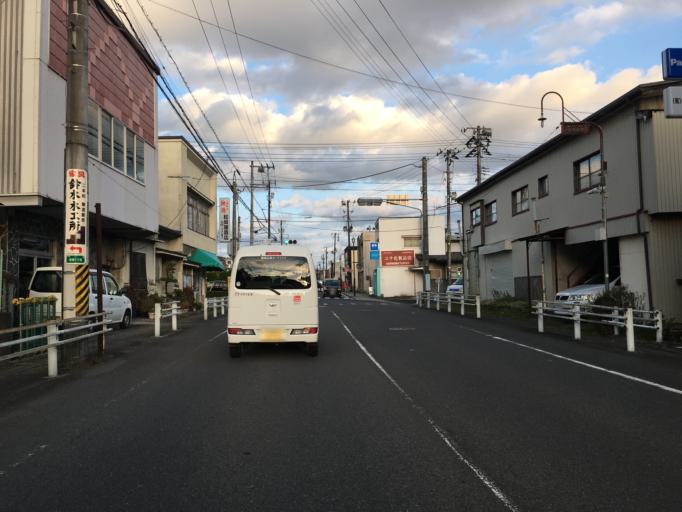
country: JP
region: Fukushima
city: Nihommatsu
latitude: 37.5914
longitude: 140.4269
